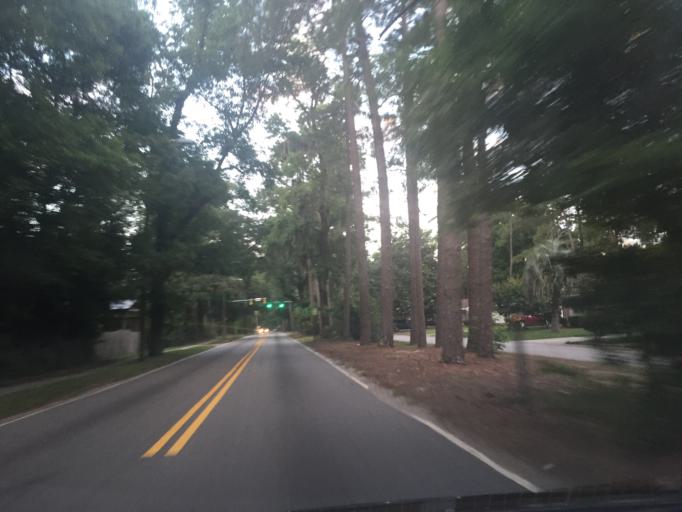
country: US
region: Georgia
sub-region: Chatham County
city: Savannah
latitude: 32.0371
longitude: -81.1081
